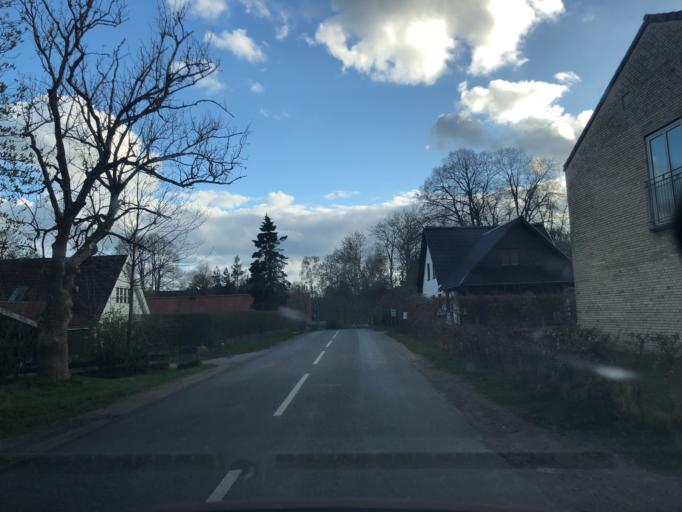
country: DK
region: Zealand
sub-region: Lejre Kommune
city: Kirke Hvalso
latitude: 55.5035
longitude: 11.8634
